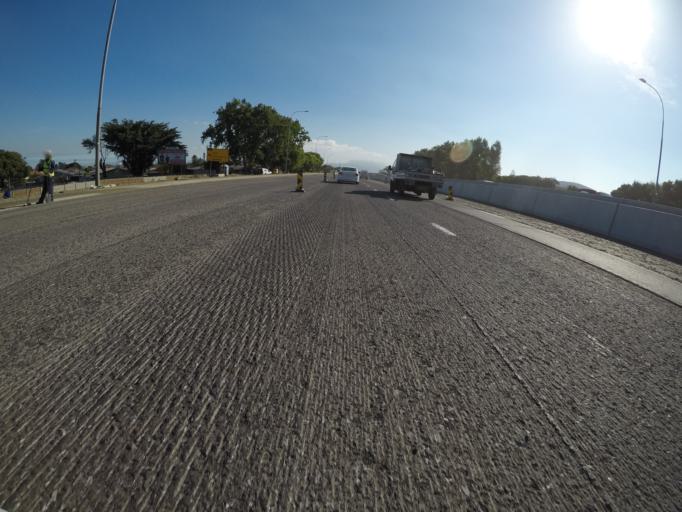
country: ZA
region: Western Cape
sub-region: City of Cape Town
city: Kraaifontein
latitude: -33.8847
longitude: 18.6408
